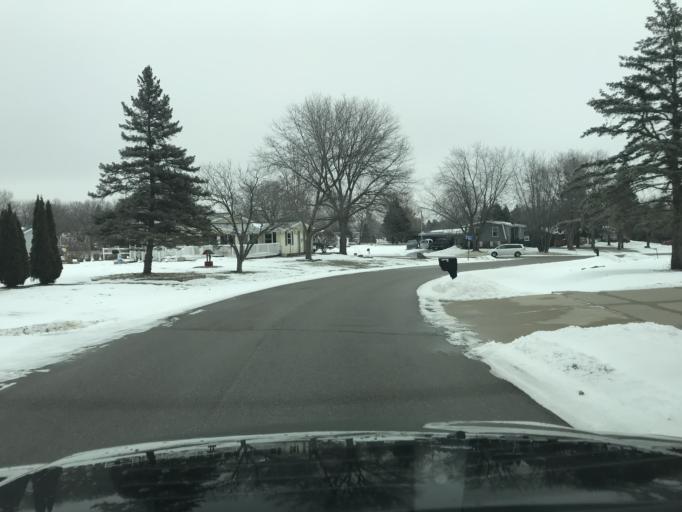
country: US
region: Wisconsin
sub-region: Dane County
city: Cottage Grove
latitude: 43.1038
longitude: -89.2169
